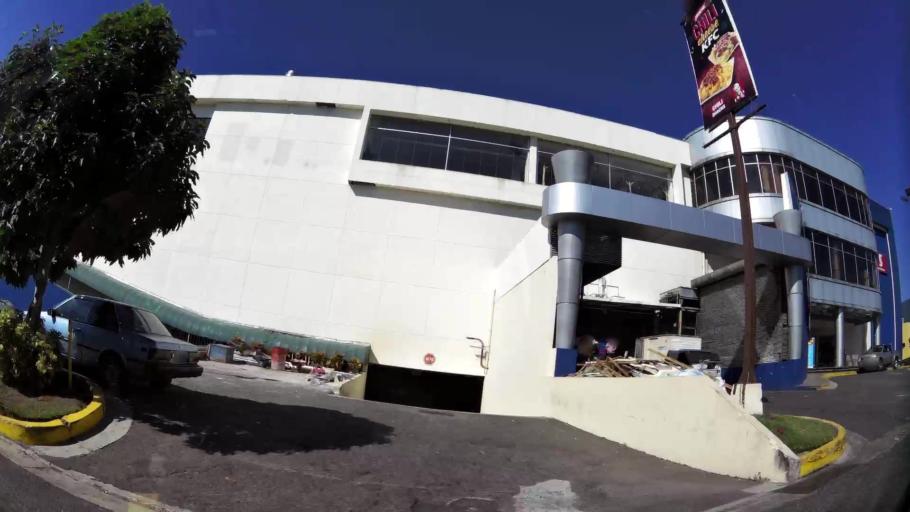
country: SV
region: La Libertad
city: Santa Tecla
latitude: 13.6787
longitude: -89.2745
